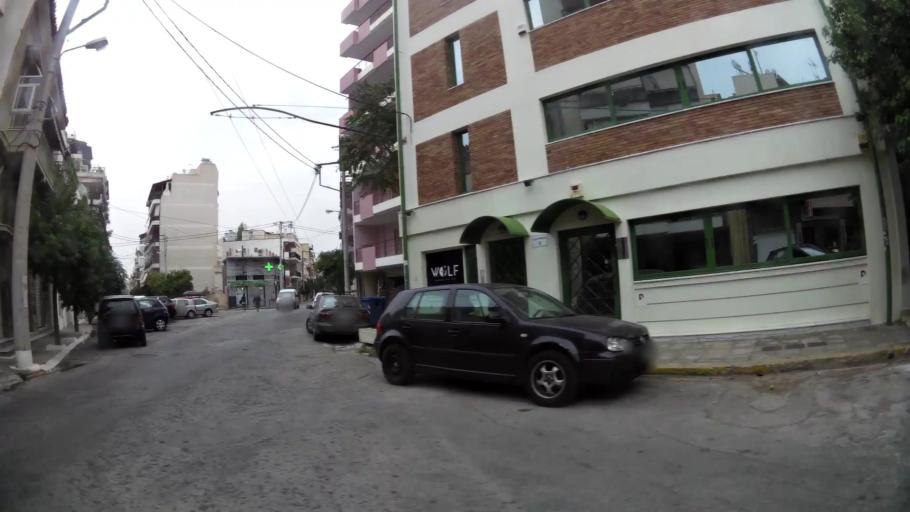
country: GR
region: Attica
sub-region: Nomos Piraios
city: Nikaia
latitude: 37.9517
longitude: 23.6540
